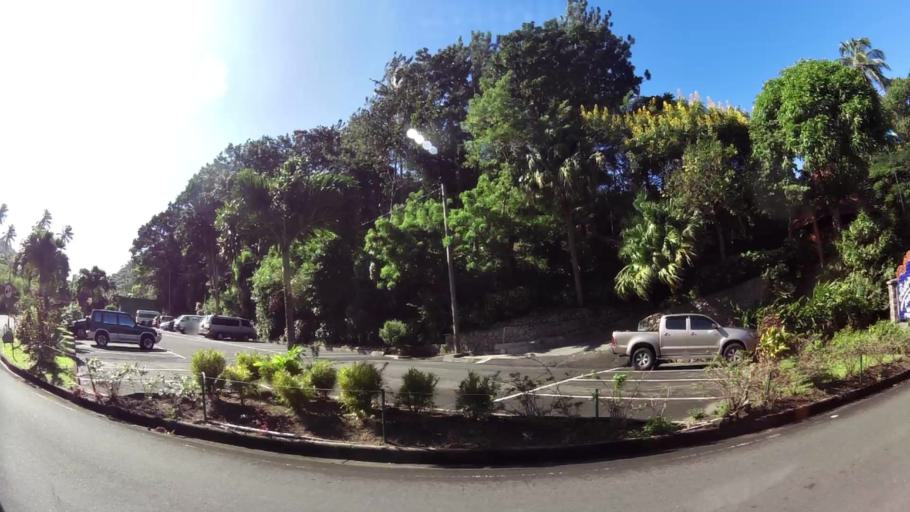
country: LC
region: Soufriere
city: Soufriere
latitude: 13.8331
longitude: -61.0511
